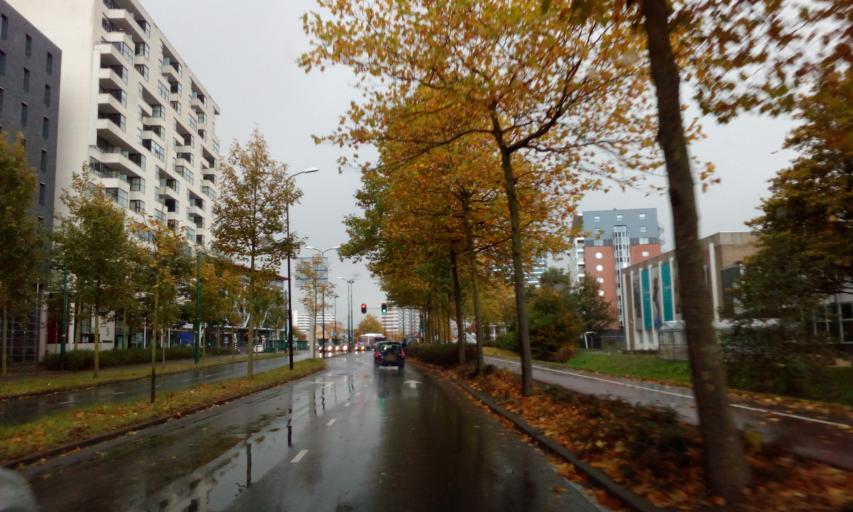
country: NL
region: South Holland
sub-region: Gemeente Rijswijk
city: Rijswijk
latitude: 52.0389
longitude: 4.3238
